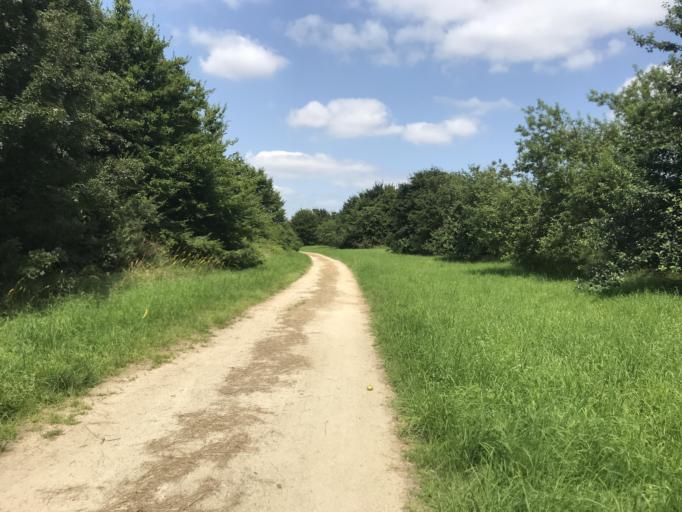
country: DE
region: Hesse
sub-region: Regierungsbezirk Darmstadt
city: Bischofsheim
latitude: 50.0134
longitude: 8.3877
